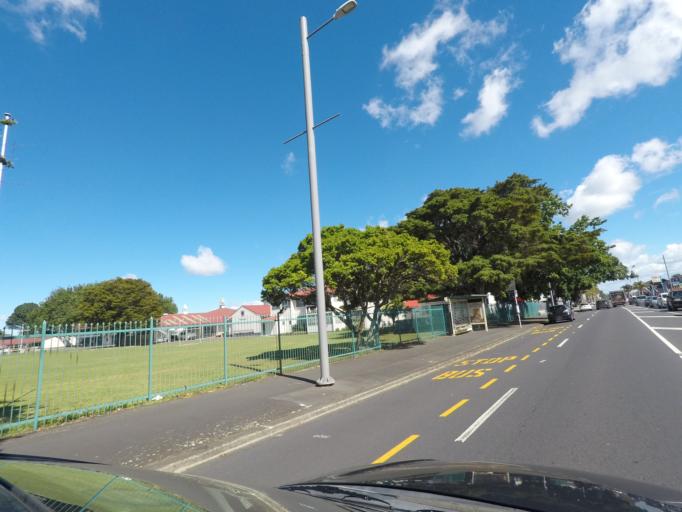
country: NZ
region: Auckland
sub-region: Auckland
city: Manukau City
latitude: -36.9736
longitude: 174.8643
